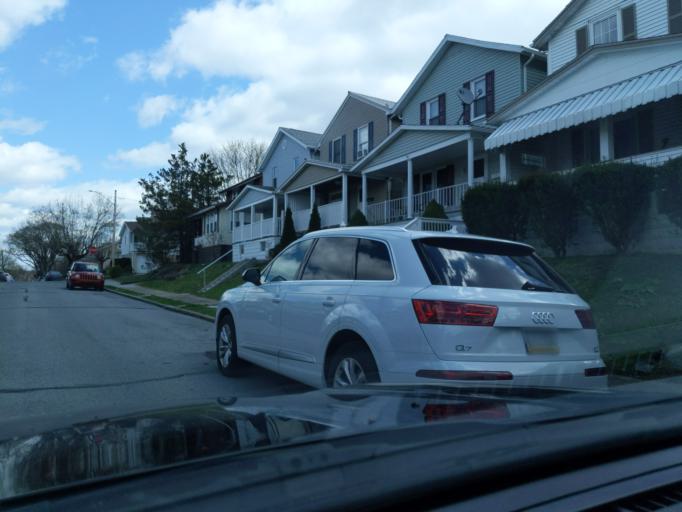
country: US
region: Pennsylvania
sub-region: Blair County
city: Altoona
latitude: 40.5316
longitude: -78.4021
